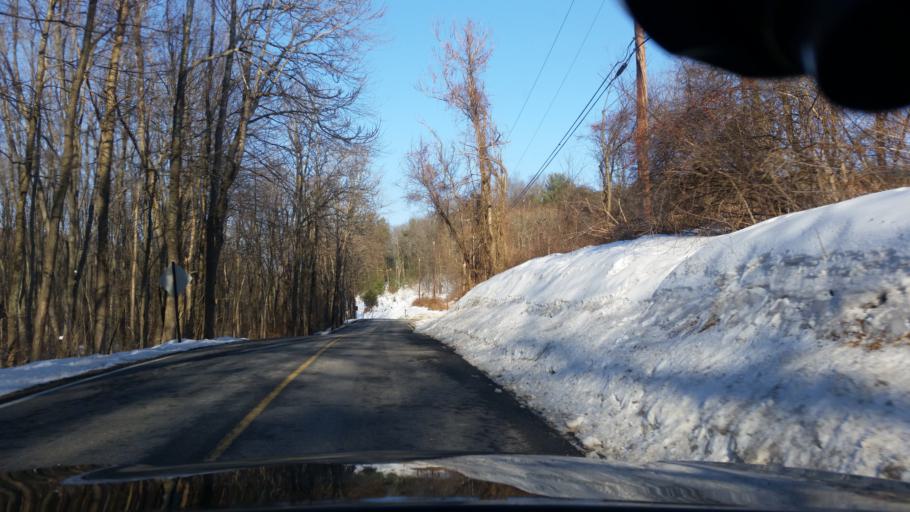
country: US
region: Pennsylvania
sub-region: Perry County
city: Marysville
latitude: 40.3252
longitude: -76.9837
